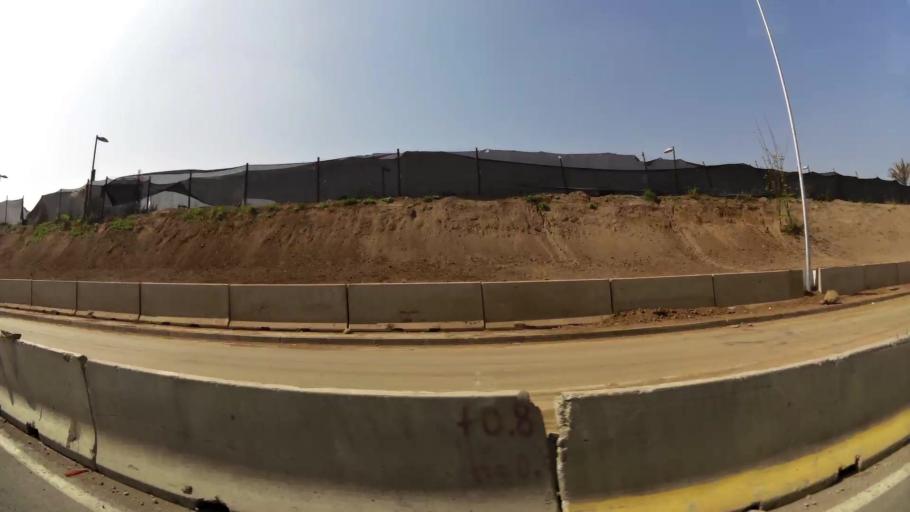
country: CL
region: Santiago Metropolitan
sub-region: Provincia de Santiago
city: Villa Presidente Frei, Nunoa, Santiago, Chile
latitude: -33.4056
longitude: -70.6032
